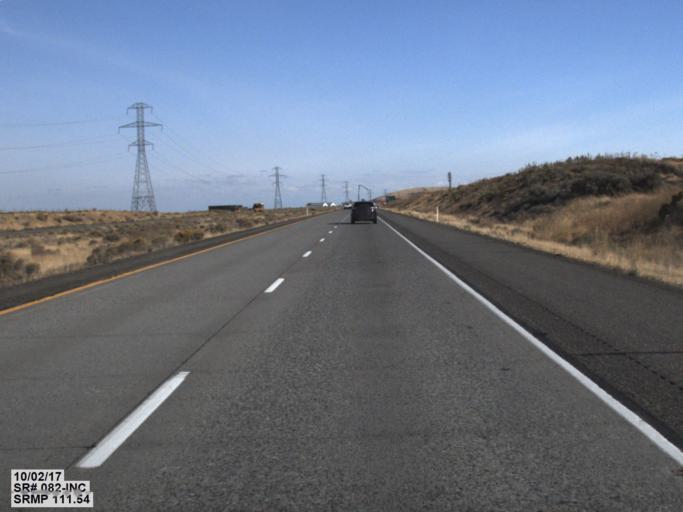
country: US
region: Washington
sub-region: Franklin County
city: West Pasco
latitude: 46.1749
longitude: -119.2229
